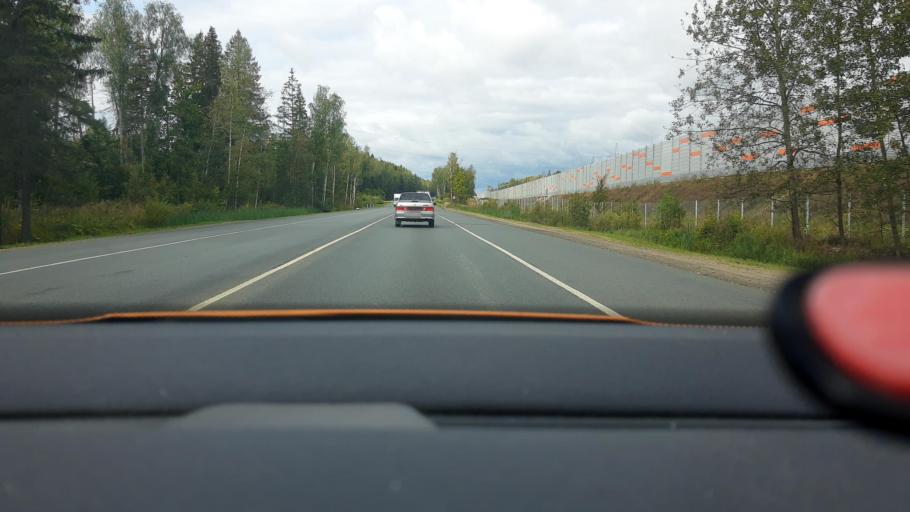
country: RU
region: Moskovskaya
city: Zelenogradskiy
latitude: 56.0869
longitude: 37.9959
